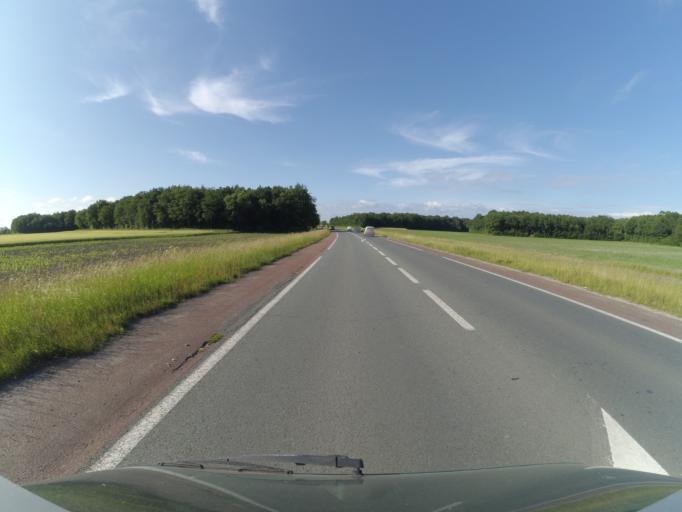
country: FR
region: Poitou-Charentes
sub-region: Departement de la Charente-Maritime
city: Saint-Sulpice-de-Royan
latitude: 45.6752
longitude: -0.9992
